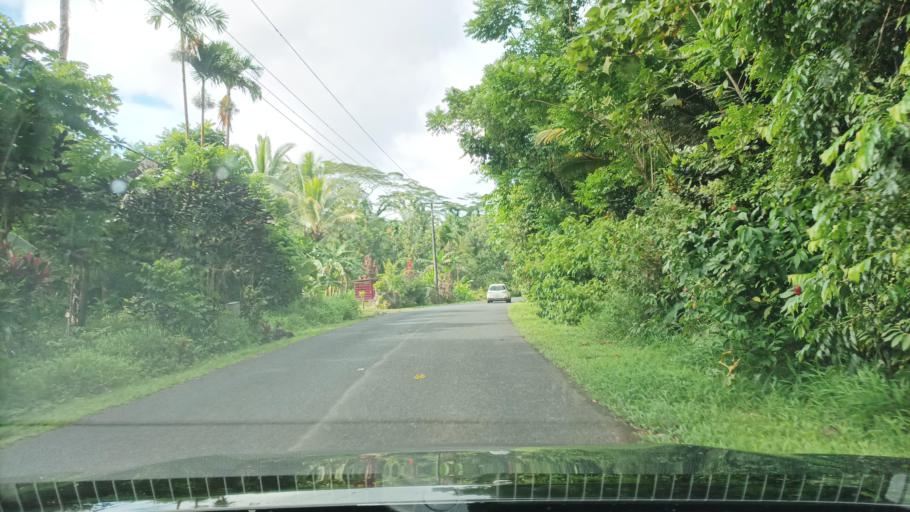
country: FM
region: Pohnpei
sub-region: Sokehs Municipality
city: Palikir - National Government Center
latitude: 6.9164
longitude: 158.1598
